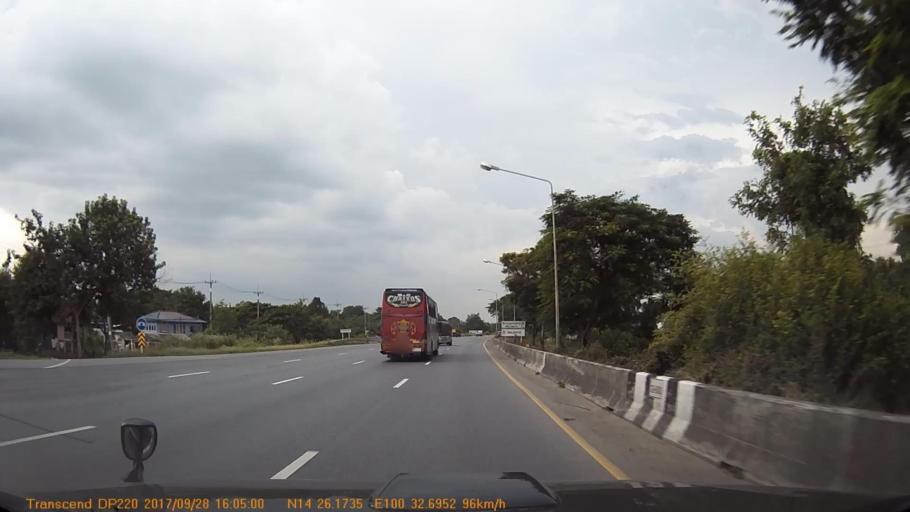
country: TH
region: Phra Nakhon Si Ayutthaya
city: Bang Pahan
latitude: 14.4367
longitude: 100.5446
